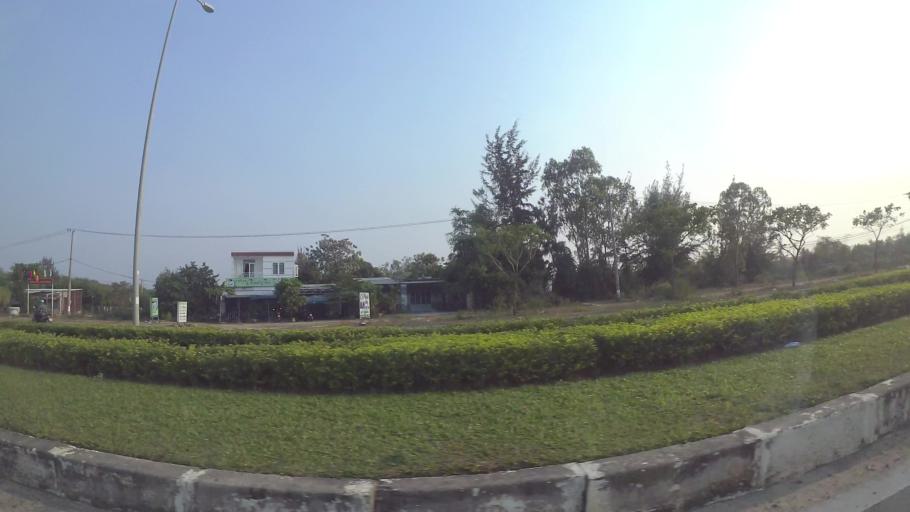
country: VN
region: Da Nang
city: Ngu Hanh Son
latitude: 15.9779
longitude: 108.2468
